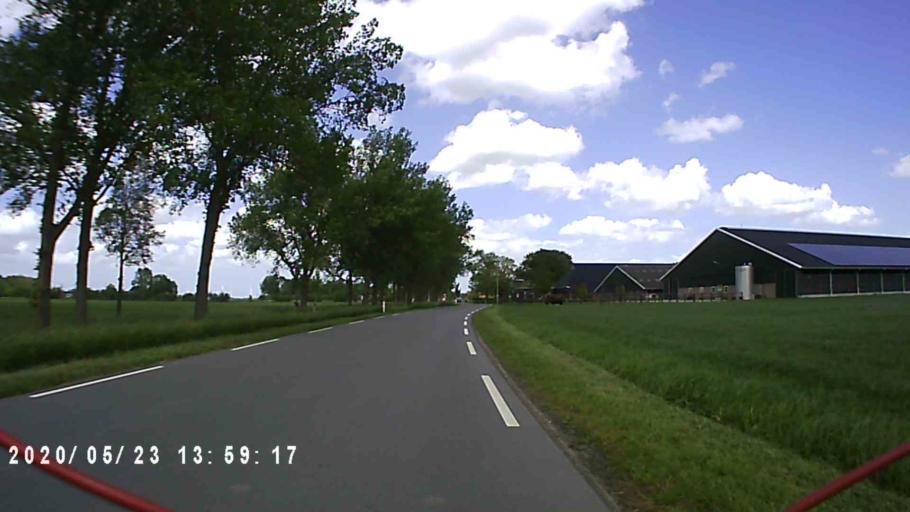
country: NL
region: Groningen
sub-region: Gemeente  Oldambt
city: Winschoten
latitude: 53.2633
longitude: 7.0260
